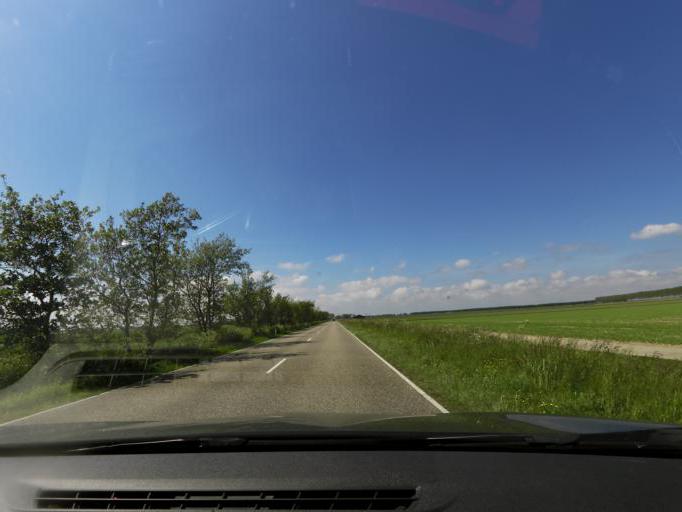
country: NL
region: South Holland
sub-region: Gemeente Goeree-Overflakkee
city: Dirksland
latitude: 51.7891
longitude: 4.0566
